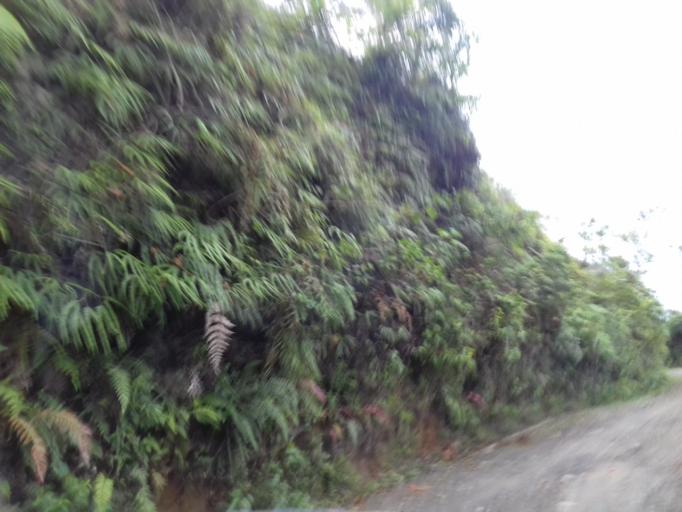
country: CO
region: Tolima
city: Libano
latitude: 4.9440
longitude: -75.0542
